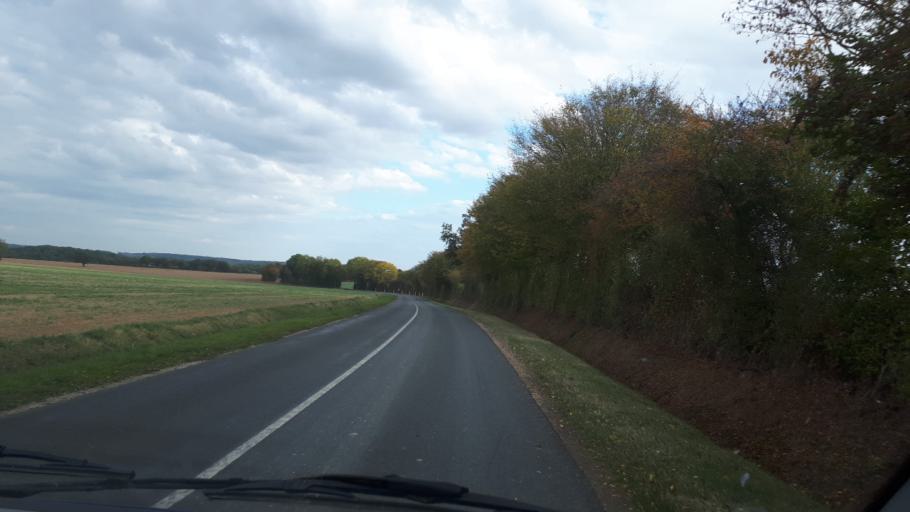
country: FR
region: Centre
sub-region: Departement du Loir-et-Cher
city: Mondoubleau
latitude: 48.0504
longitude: 0.9438
